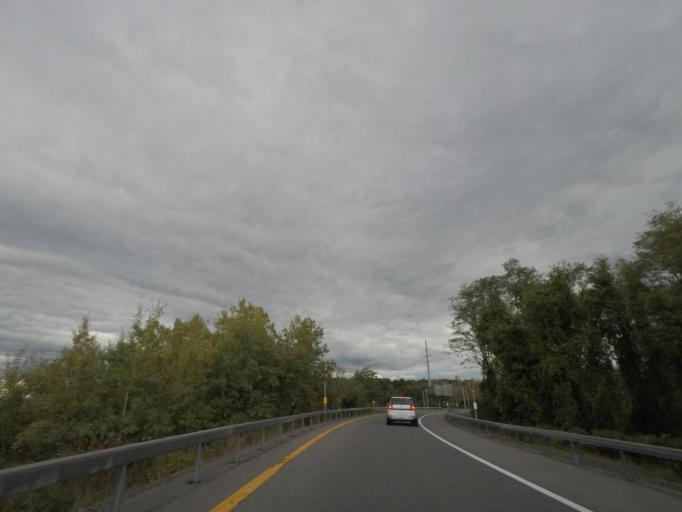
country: US
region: New York
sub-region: Albany County
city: McKownville
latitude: 42.6932
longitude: -73.8411
